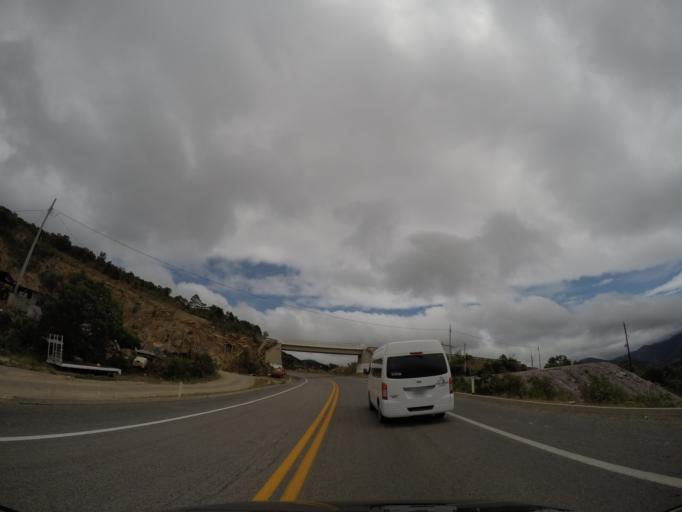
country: MX
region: Oaxaca
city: San Lorenzo Albarradas
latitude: 16.9281
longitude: -96.2603
